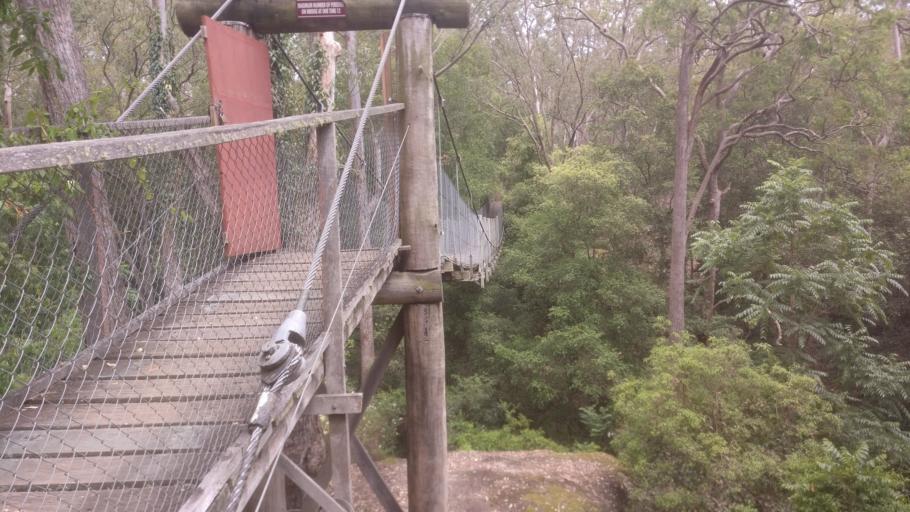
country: AU
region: New South Wales
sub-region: Shoalhaven Shire
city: Kangaroo Valley
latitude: -34.7264
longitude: 150.5191
